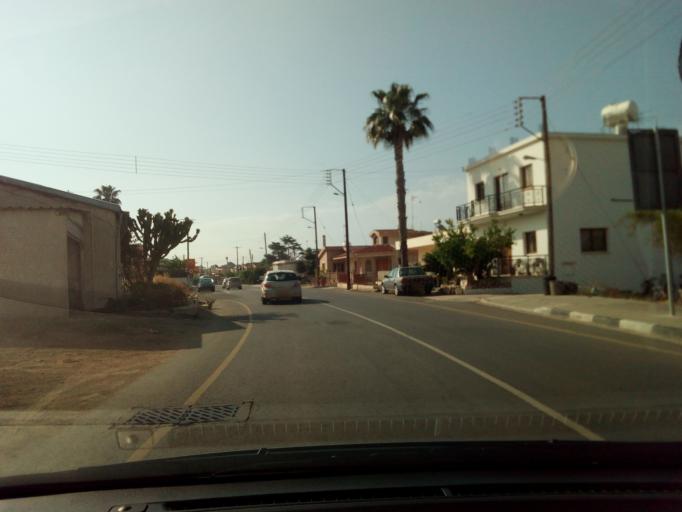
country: CY
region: Larnaka
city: Xylotymbou
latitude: 34.9946
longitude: 33.7722
